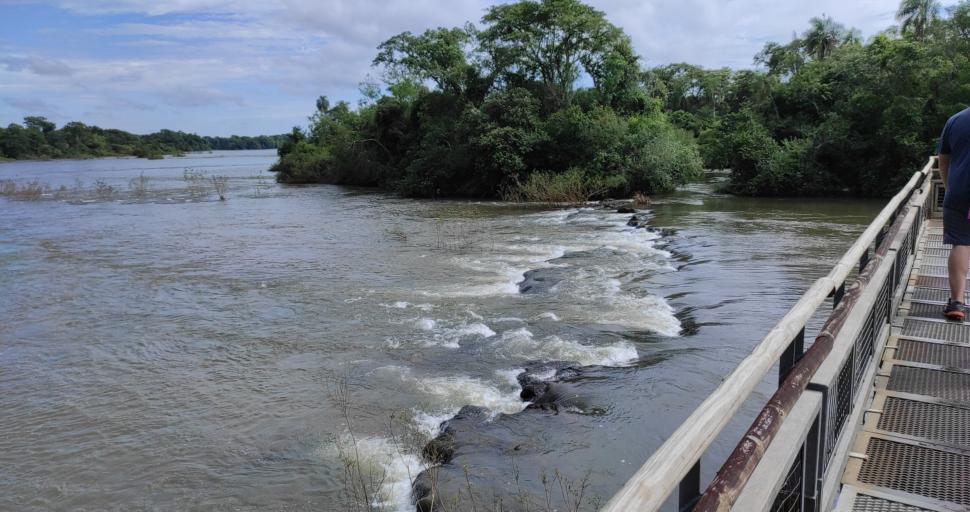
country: AR
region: Misiones
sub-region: Departamento de Iguazu
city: Puerto Iguazu
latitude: -25.7004
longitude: -54.4434
